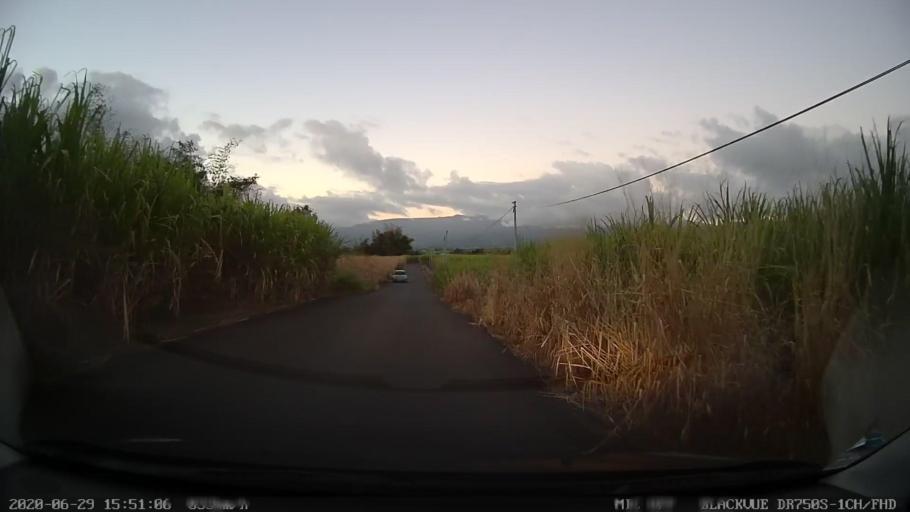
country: RE
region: Reunion
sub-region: Reunion
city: Bras-Panon
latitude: -20.9924
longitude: 55.6933
